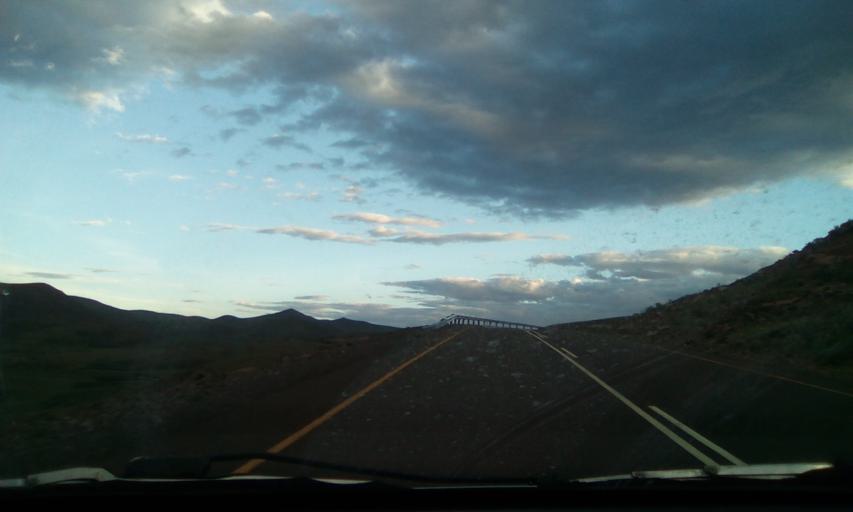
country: LS
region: Maseru
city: Nako
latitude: -29.8148
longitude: 28.0337
